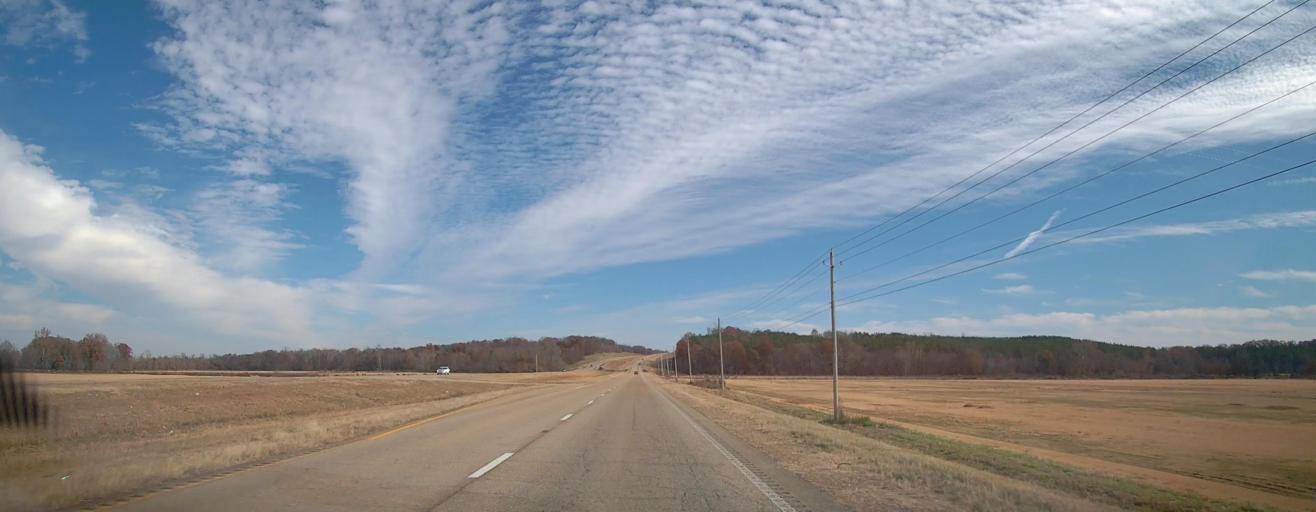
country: US
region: Mississippi
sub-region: Alcorn County
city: Corinth
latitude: 34.9318
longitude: -88.6592
